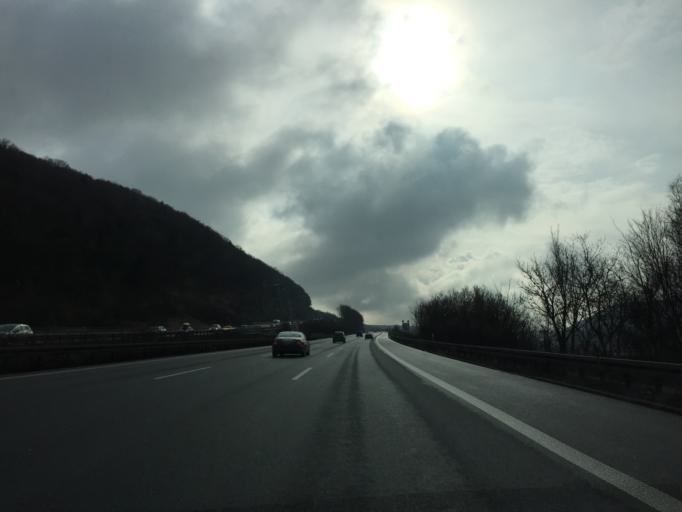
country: DE
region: Bavaria
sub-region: Regierungsbezirk Mittelfranken
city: Greding
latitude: 48.9912
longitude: 11.3834
